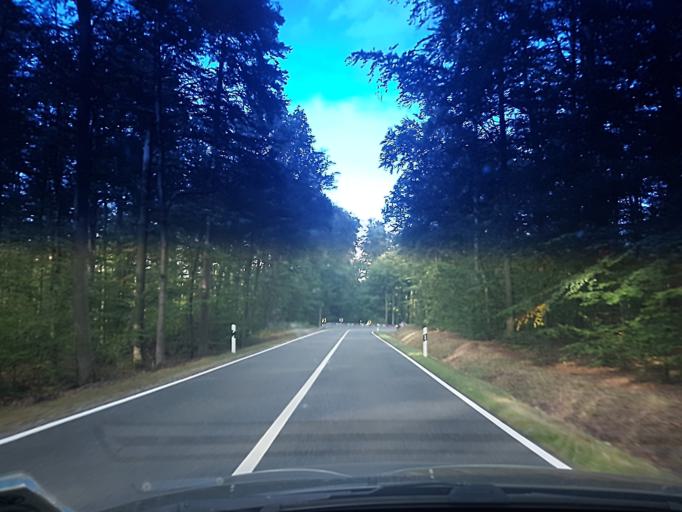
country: DE
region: Bavaria
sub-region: Upper Franconia
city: Burgwindheim
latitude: 49.7988
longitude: 10.5751
